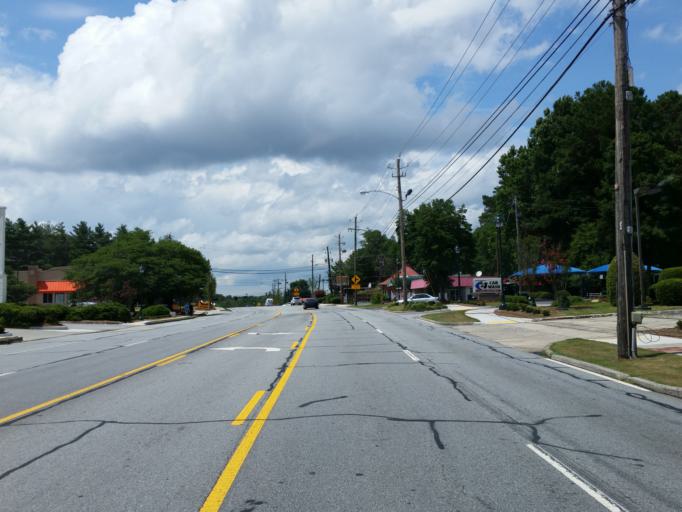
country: US
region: Georgia
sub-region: Fulton County
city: Roswell
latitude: 33.9863
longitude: -84.3507
